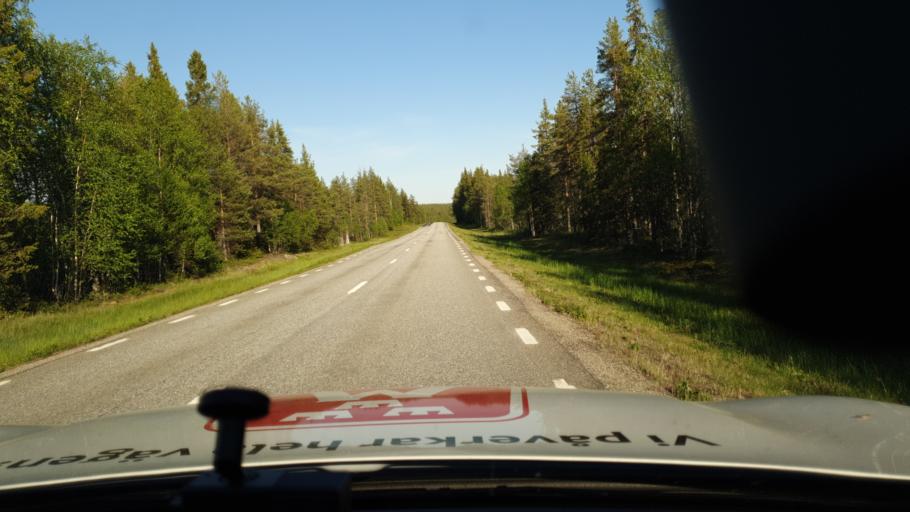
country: SE
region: Vaesterbotten
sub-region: Lycksele Kommun
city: Soderfors
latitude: 64.6918
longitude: 17.7689
